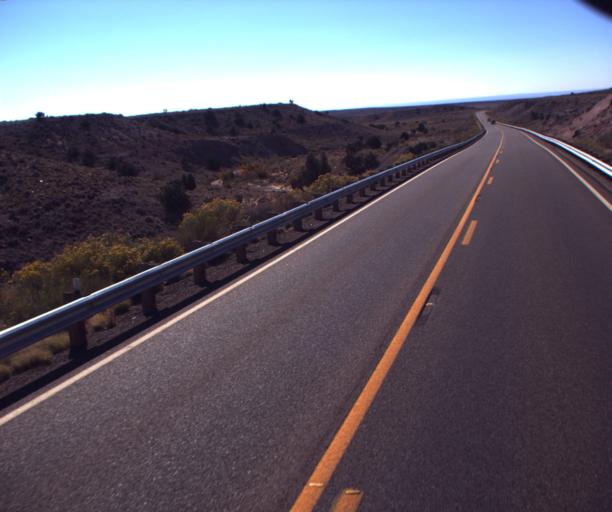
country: US
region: Arizona
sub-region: Navajo County
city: Dilkon
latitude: 35.1850
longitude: -110.4429
